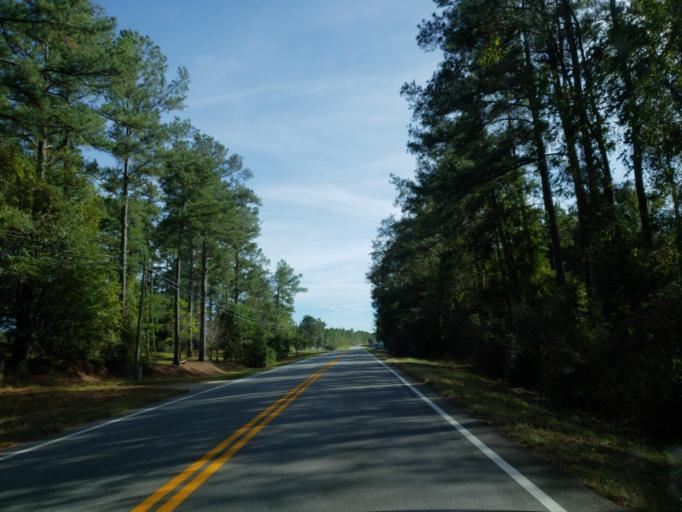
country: US
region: Georgia
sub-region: Crawford County
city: Roberta
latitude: 32.7060
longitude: -84.0098
